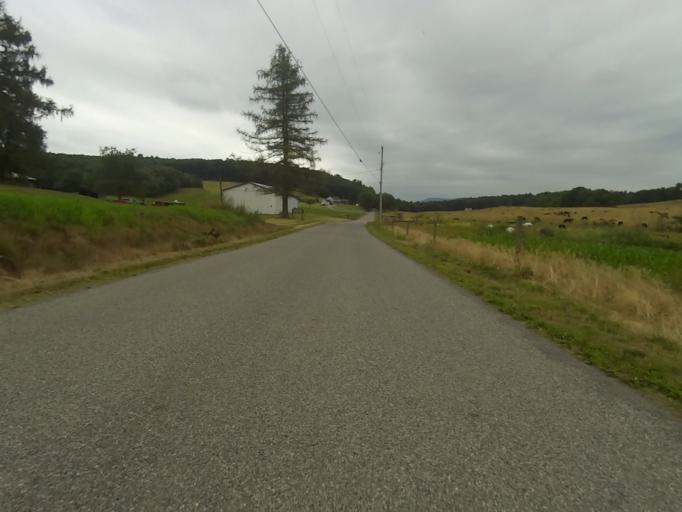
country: US
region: Pennsylvania
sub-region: Centre County
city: Stormstown
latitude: 40.6920
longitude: -78.0978
